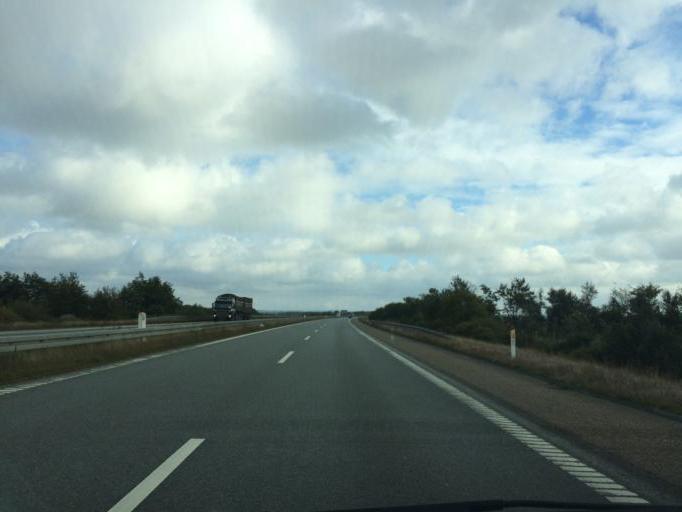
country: DK
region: North Denmark
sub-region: Bronderslev Kommune
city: Hjallerup
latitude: 57.1444
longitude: 10.1049
